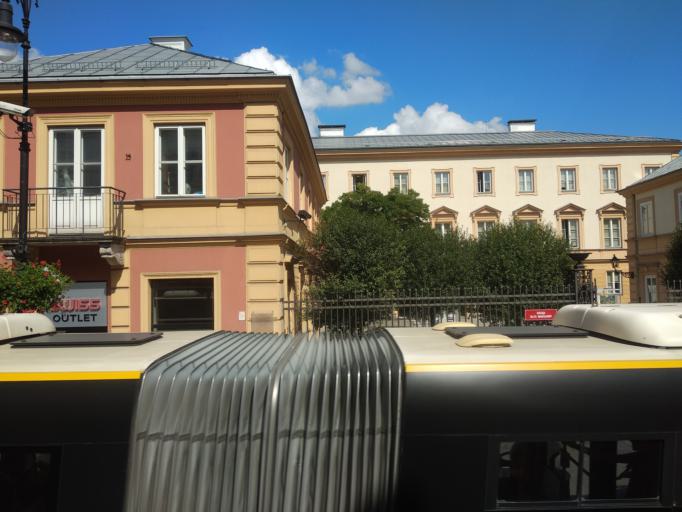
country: PL
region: Masovian Voivodeship
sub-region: Warszawa
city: Srodmiescie
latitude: 52.2325
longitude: 21.0200
